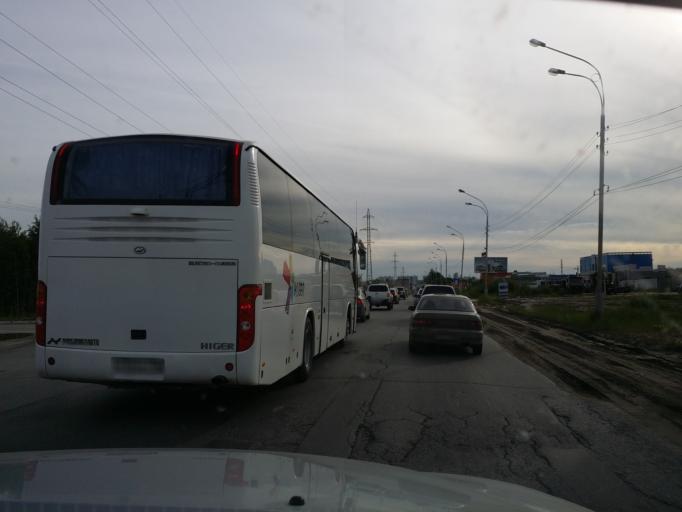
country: RU
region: Khanty-Mansiyskiy Avtonomnyy Okrug
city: Nizhnevartovsk
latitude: 60.9455
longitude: 76.6500
